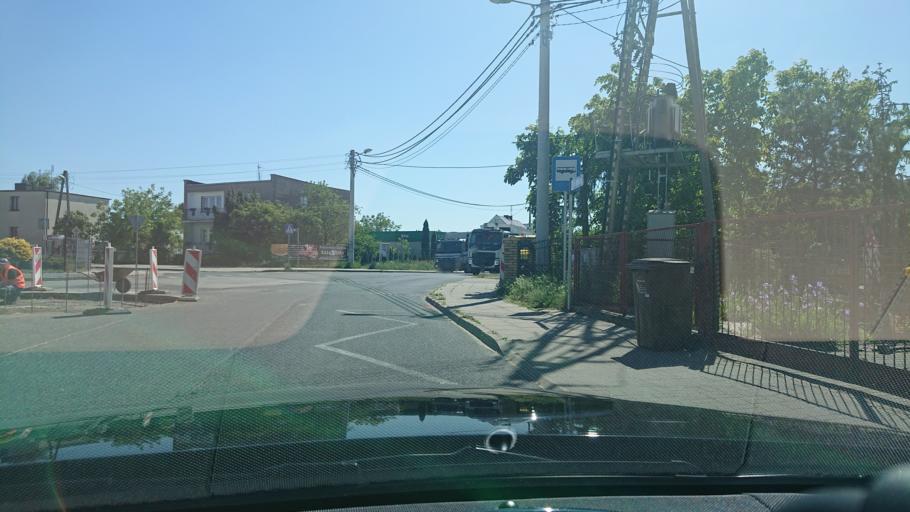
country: PL
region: Greater Poland Voivodeship
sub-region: Powiat gnieznienski
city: Gniezno
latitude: 52.5040
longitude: 17.5873
